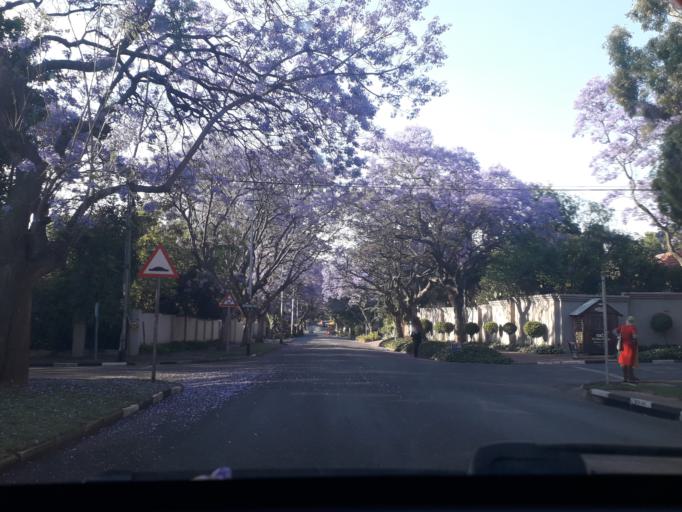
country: ZA
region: Gauteng
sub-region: City of Johannesburg Metropolitan Municipality
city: Johannesburg
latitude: -26.1515
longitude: 28.0417
